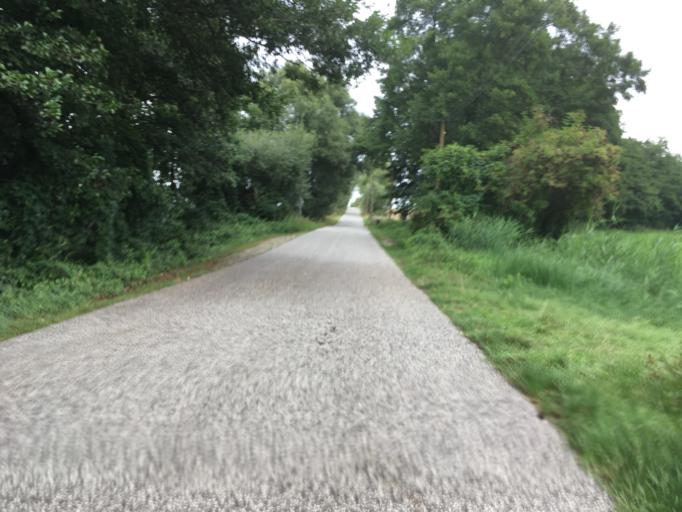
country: DE
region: Brandenburg
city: Gerswalde
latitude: 53.1673
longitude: 13.8458
